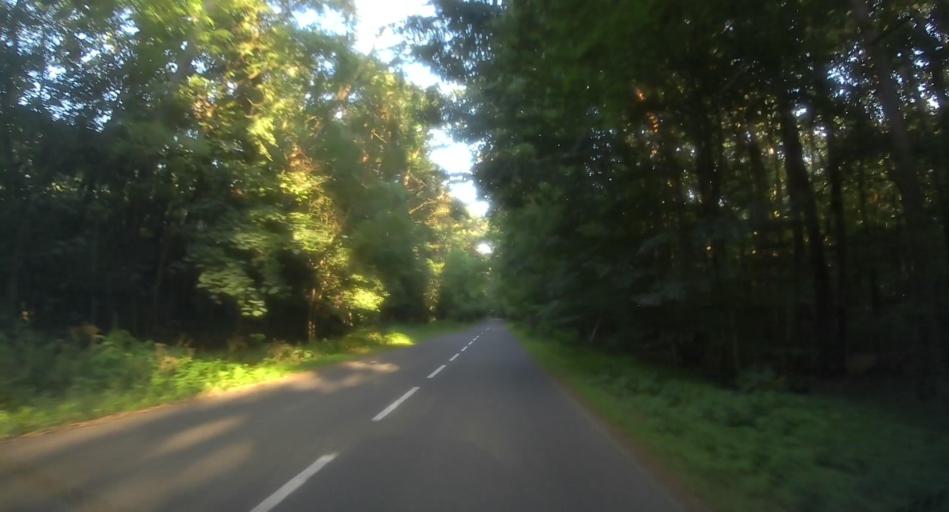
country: PL
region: Lodz Voivodeship
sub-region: Powiat skierniewicki
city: Kowiesy
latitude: 51.8911
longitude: 20.3954
